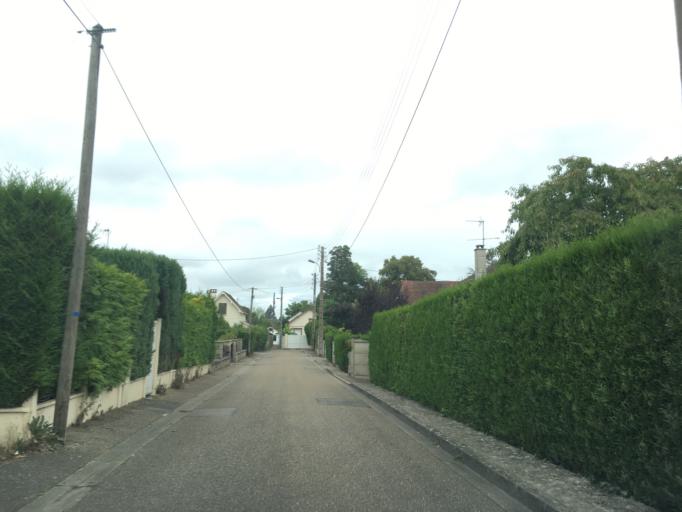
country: FR
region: Haute-Normandie
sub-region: Departement de l'Eure
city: Vernon
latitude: 49.0863
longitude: 1.4756
